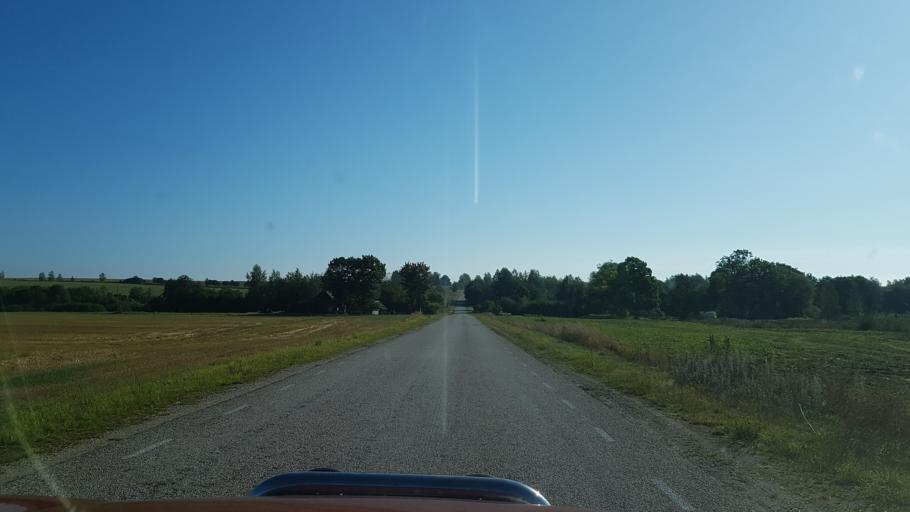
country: EE
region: Jogevamaa
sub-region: Tabivere vald
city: Tabivere
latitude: 58.6740
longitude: 26.7080
